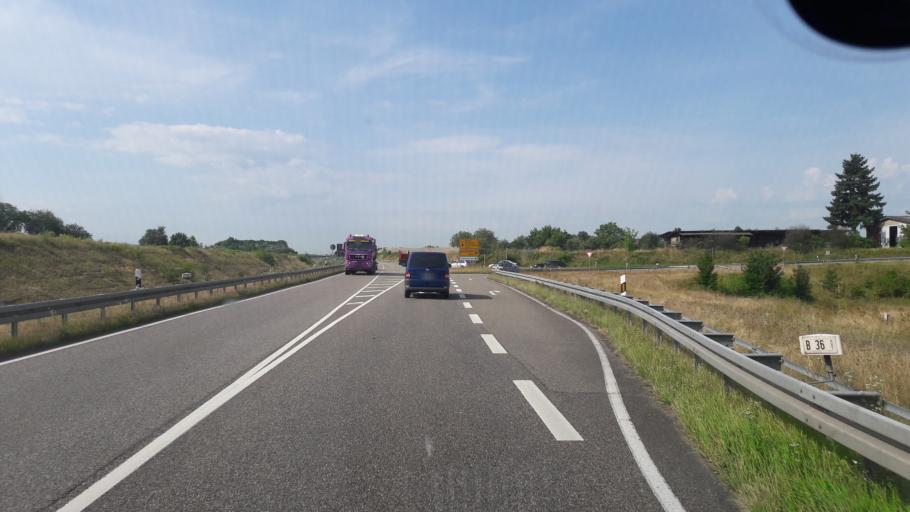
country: DE
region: Baden-Wuerttemberg
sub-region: Karlsruhe Region
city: Durmersheim
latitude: 48.9368
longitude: 8.2833
